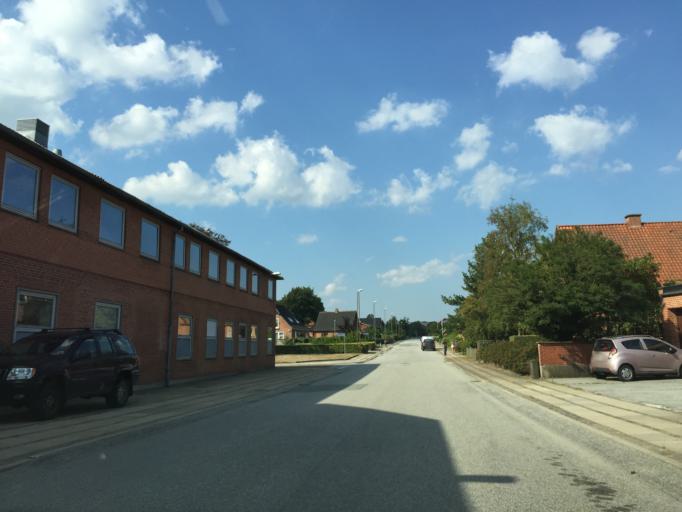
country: DK
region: Central Jutland
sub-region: Viborg Kommune
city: Bjerringbro
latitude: 56.3763
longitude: 9.6662
